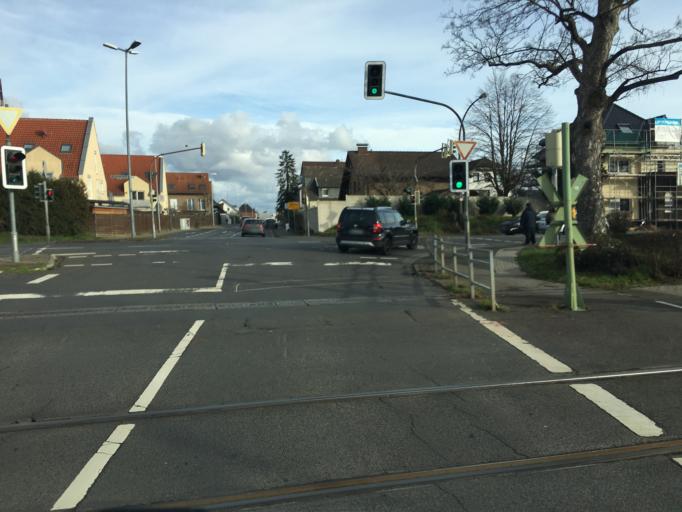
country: DE
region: North Rhine-Westphalia
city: Niederkassel
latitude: 50.8043
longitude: 7.0099
